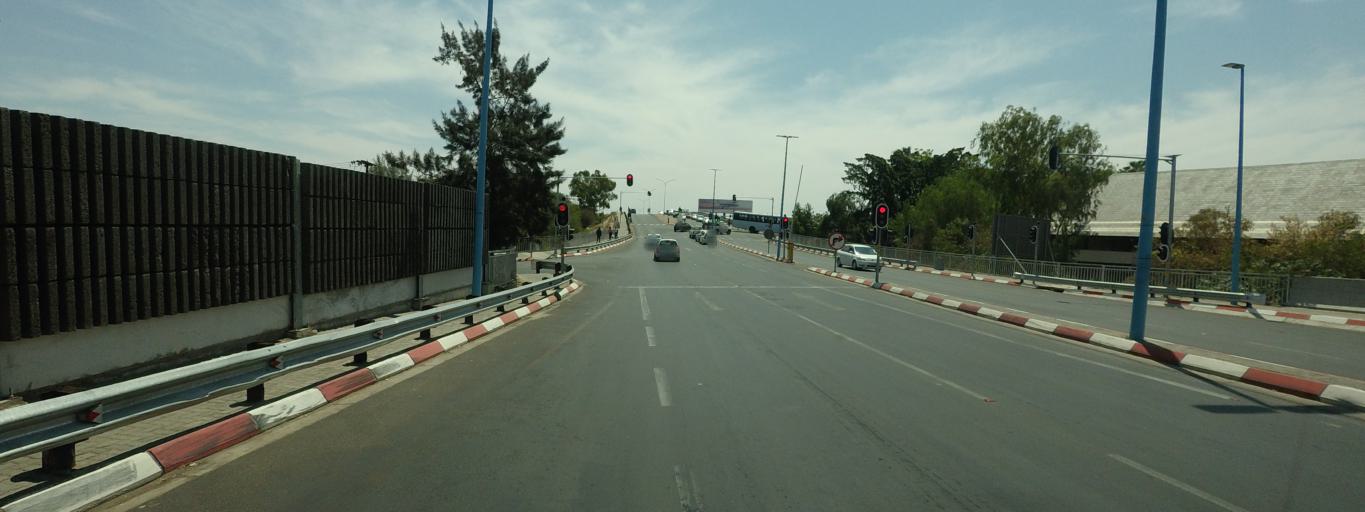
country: BW
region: North East
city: Francistown
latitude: -21.1735
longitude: 27.5115
